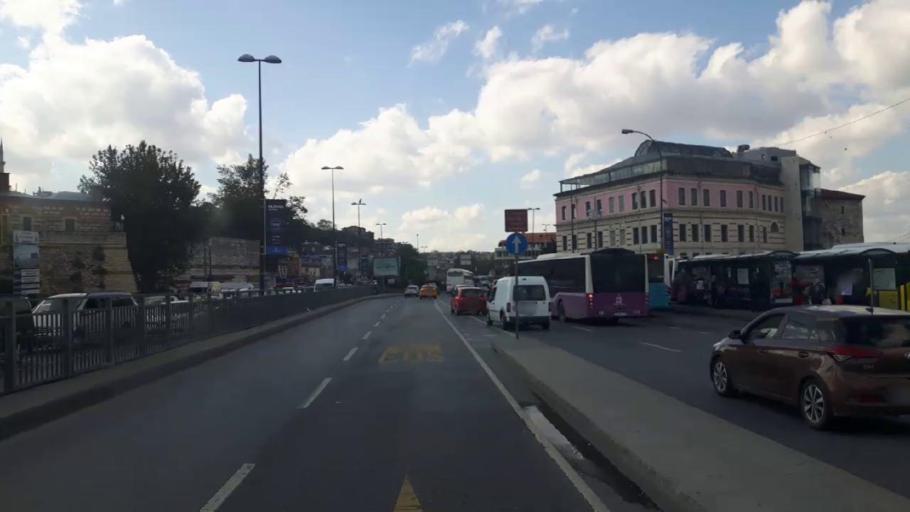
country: TR
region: Istanbul
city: Eminoenue
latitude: 41.0180
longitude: 28.9703
